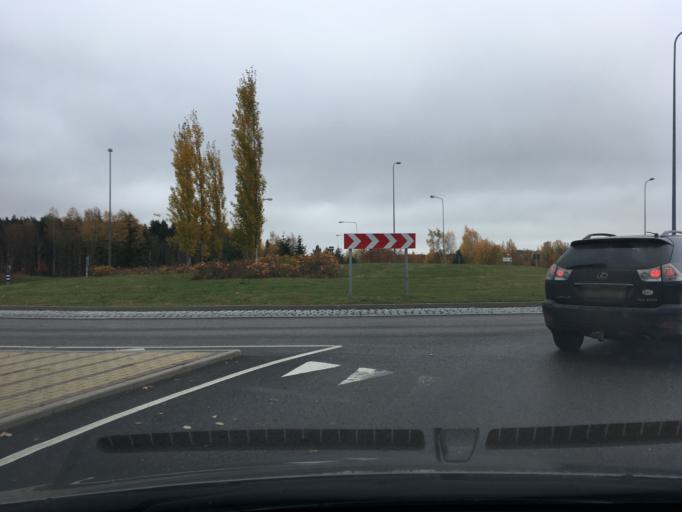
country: EE
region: Tartu
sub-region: Tartu linn
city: Tartu
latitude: 58.3632
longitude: 26.7724
